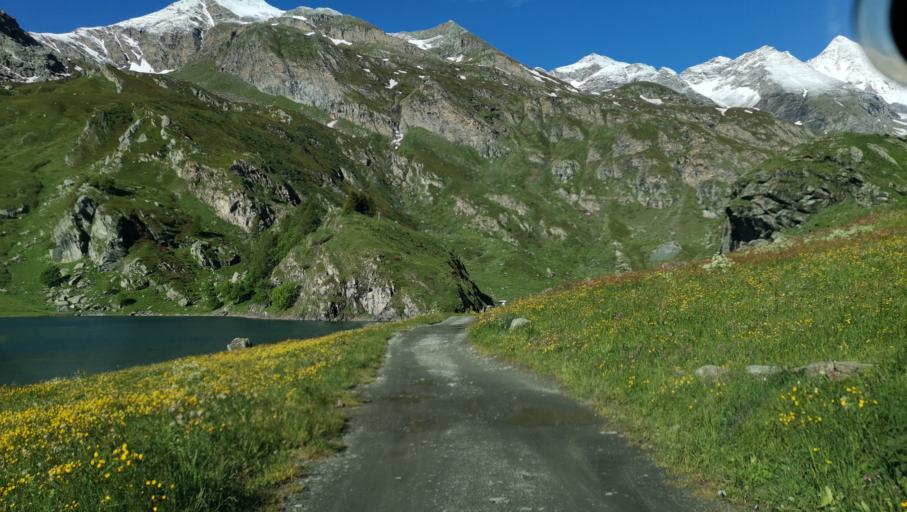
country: IT
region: Piedmont
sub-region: Provincia di Torino
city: Chianocco
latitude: 45.2086
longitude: 7.1409
